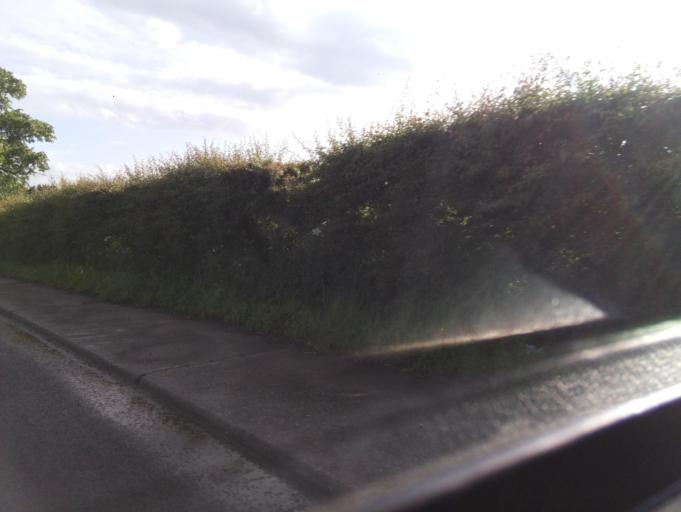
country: GB
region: England
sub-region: Lincolnshire
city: Navenby
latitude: 53.0632
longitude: -0.6372
